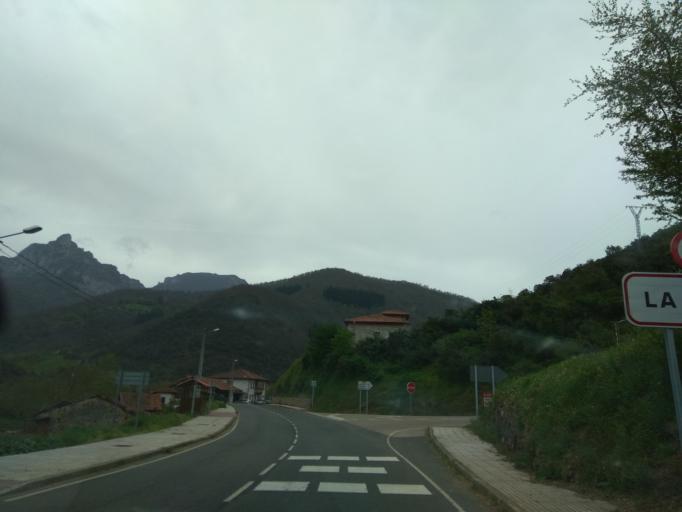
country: ES
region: Cantabria
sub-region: Provincia de Cantabria
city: Potes
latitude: 43.1019
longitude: -4.6455
